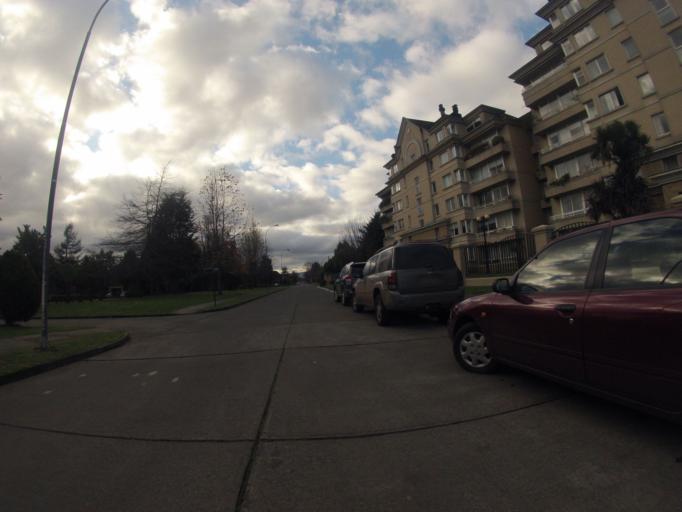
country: CL
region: Araucania
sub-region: Provincia de Cautin
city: Temuco
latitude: -38.7403
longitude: -72.6390
